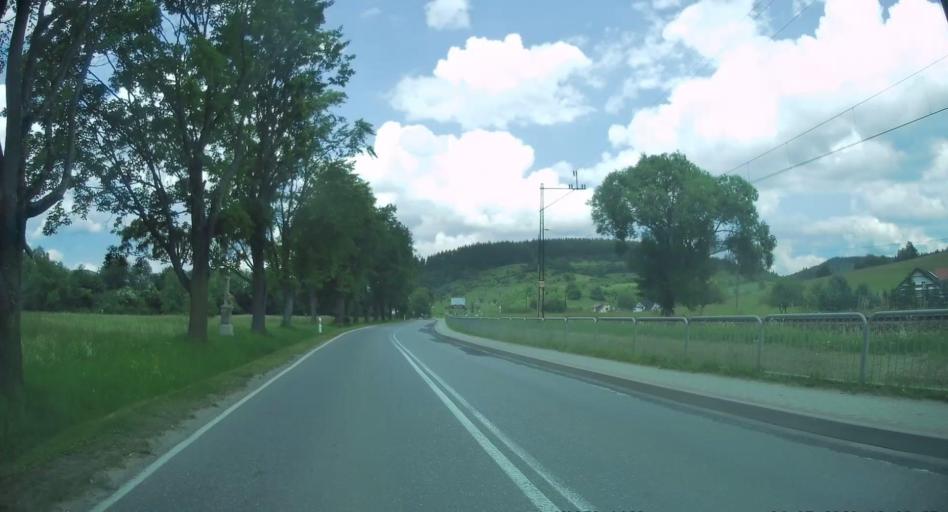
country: PL
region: Lesser Poland Voivodeship
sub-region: Powiat nowosadecki
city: Krynica-Zdroj
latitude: 49.3785
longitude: 20.9510
